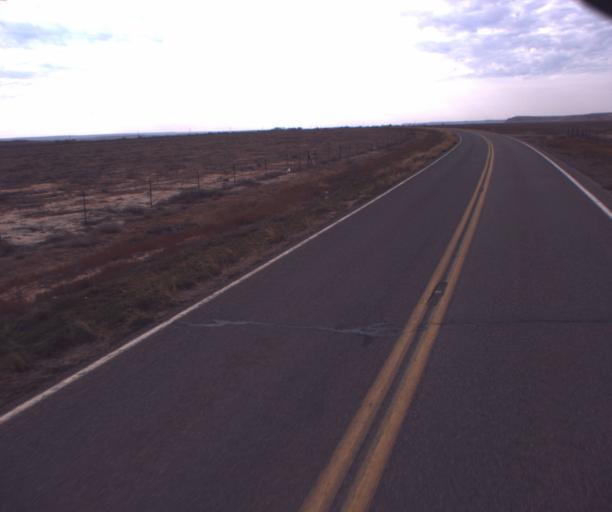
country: US
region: Arizona
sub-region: Apache County
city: Many Farms
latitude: 36.4563
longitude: -109.6077
